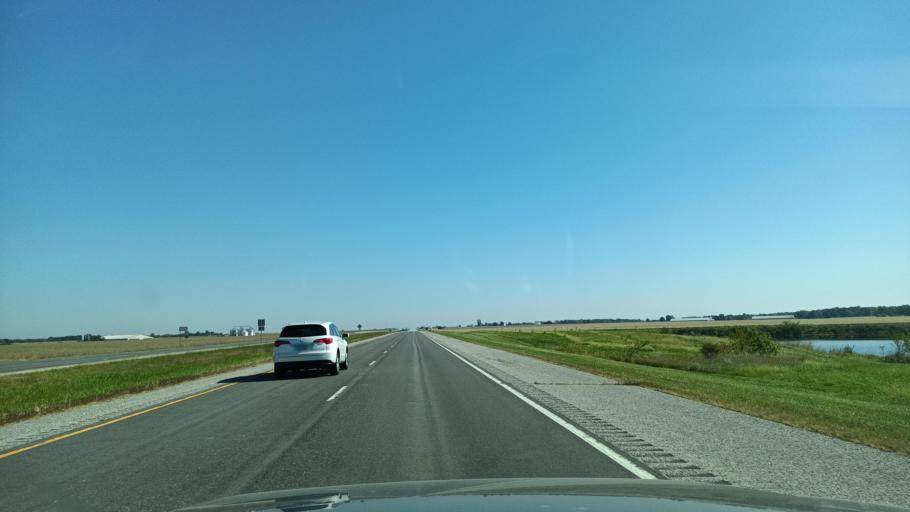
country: US
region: Illinois
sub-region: Adams County
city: Camp Point
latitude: 40.1891
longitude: -91.1744
